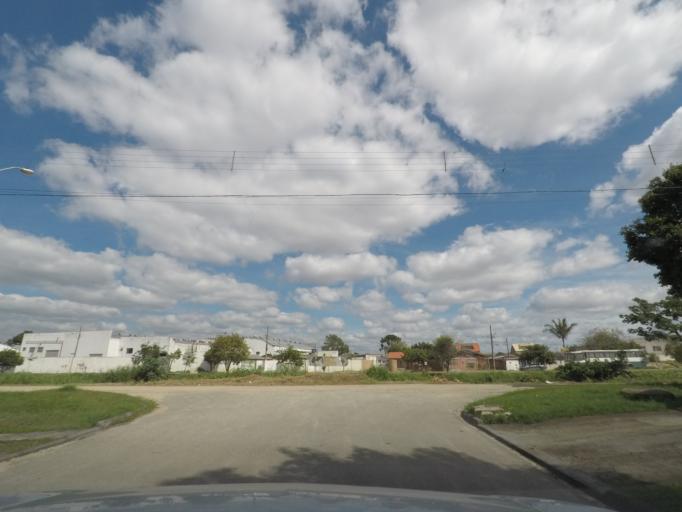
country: BR
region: Parana
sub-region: Sao Jose Dos Pinhais
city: Sao Jose dos Pinhais
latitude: -25.5045
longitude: -49.2171
